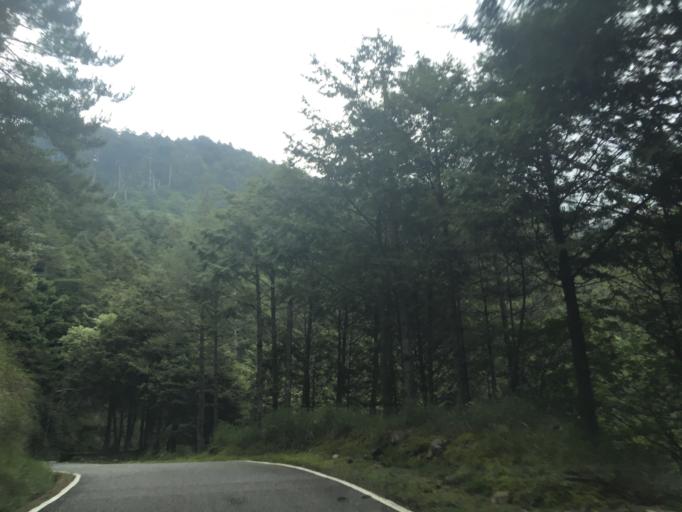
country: TW
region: Taiwan
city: Fengyuan
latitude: 24.2634
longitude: 121.0145
